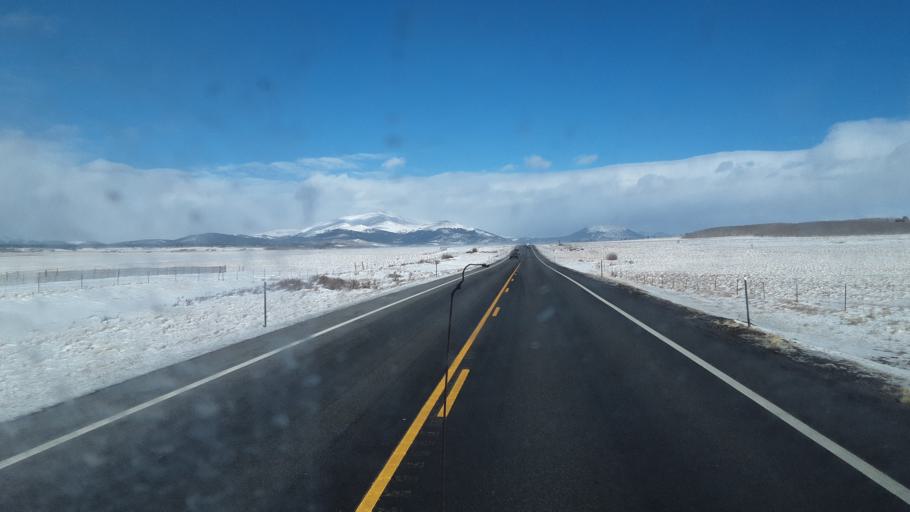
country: US
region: Colorado
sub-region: Park County
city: Fairplay
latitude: 39.1793
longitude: -105.9999
